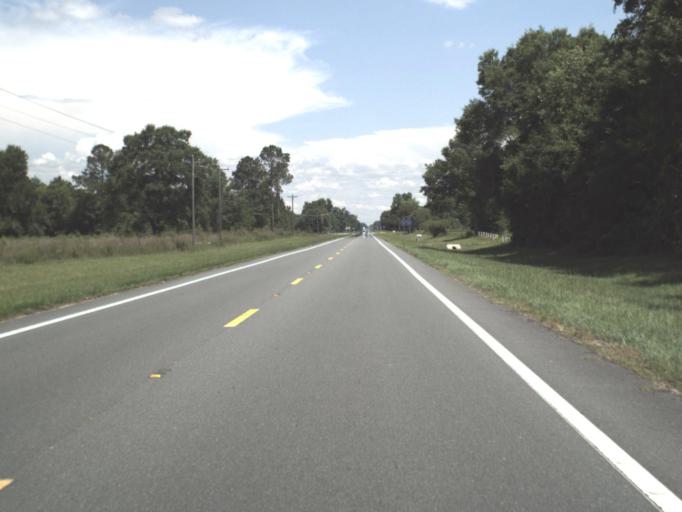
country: US
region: Florida
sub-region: Lafayette County
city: Mayo
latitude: 30.1181
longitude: -83.2614
